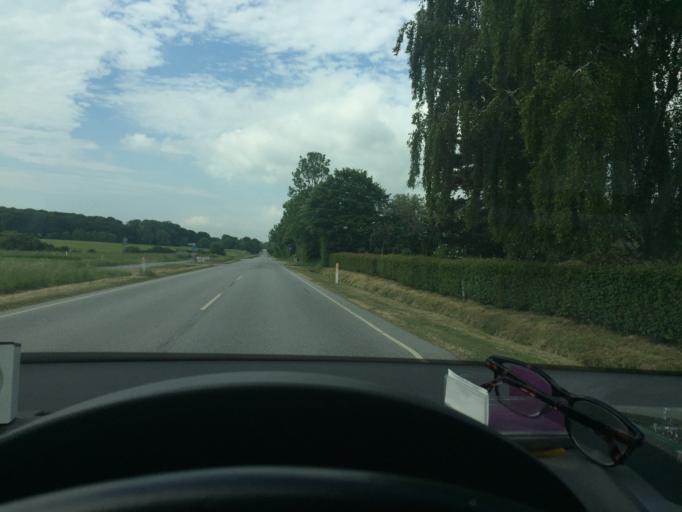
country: DK
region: South Denmark
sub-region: Haderslev Kommune
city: Starup
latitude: 55.2502
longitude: 9.5900
